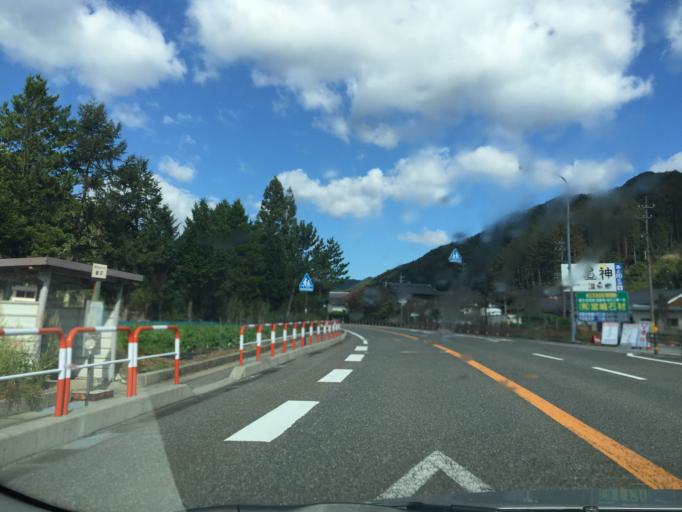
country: JP
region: Gifu
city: Nakatsugawa
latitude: 35.3251
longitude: 137.6345
